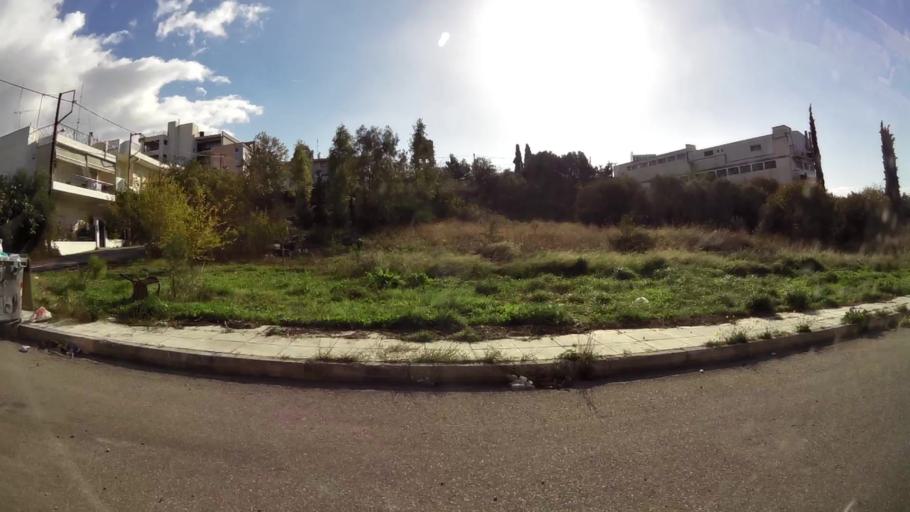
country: GR
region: Attica
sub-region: Nomarchia Anatolikis Attikis
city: Acharnes
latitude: 38.0732
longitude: 23.7376
